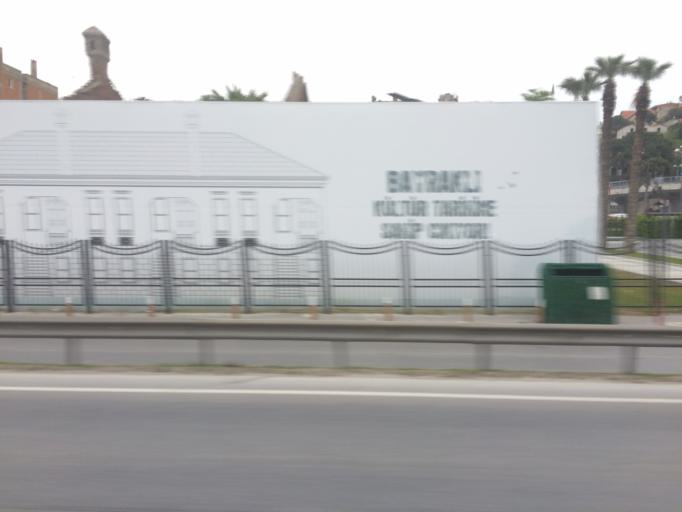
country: TR
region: Izmir
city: Karsiyaka
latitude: 38.4650
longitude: 27.1621
